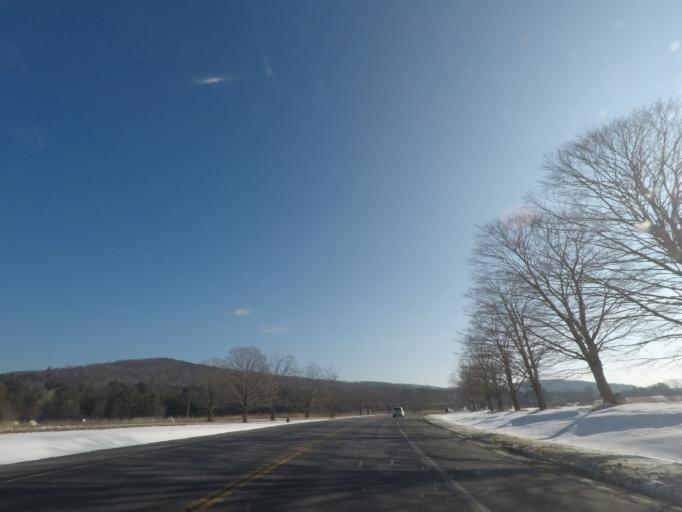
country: US
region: Massachusetts
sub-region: Berkshire County
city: Lanesborough
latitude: 42.5303
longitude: -73.3566
